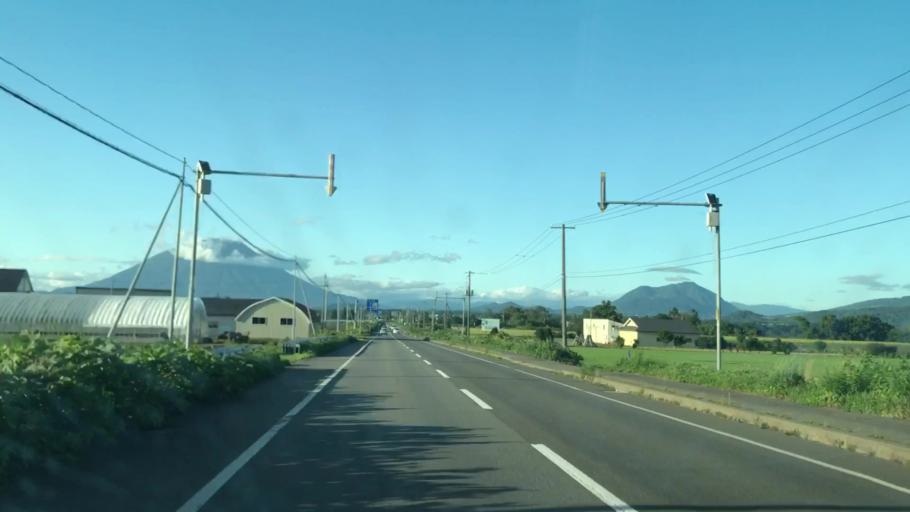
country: JP
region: Hokkaido
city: Date
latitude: 42.6383
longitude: 140.8023
